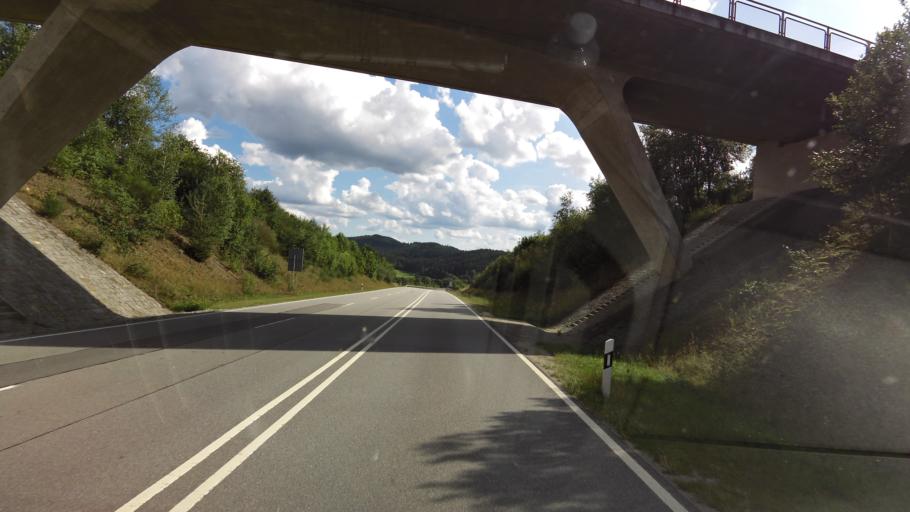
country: DE
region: Bavaria
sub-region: Upper Palatinate
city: Traitsching
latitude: 49.1589
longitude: 12.6549
